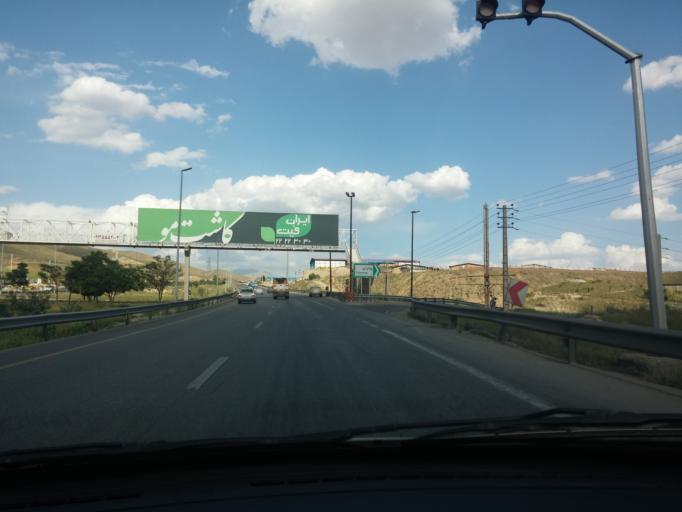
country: IR
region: Tehran
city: Damavand
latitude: 35.7076
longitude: 51.9710
